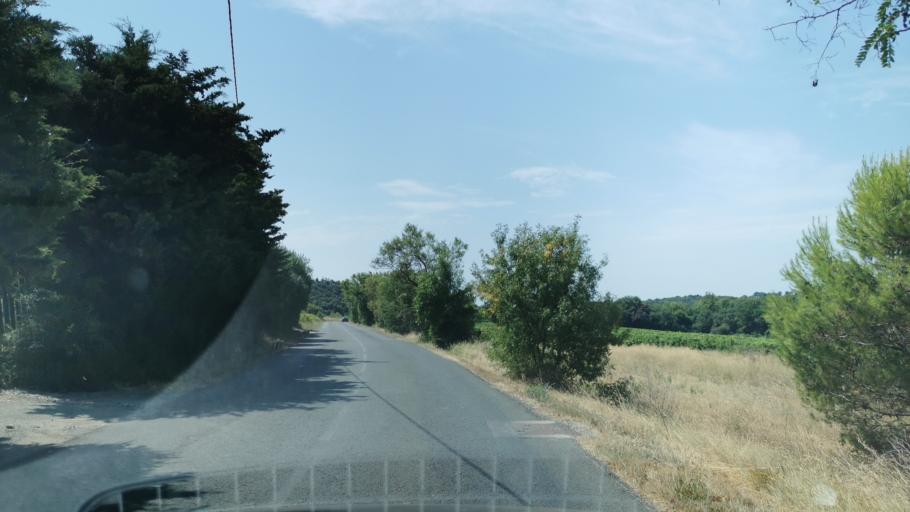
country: FR
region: Languedoc-Roussillon
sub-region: Departement de l'Aude
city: Bize-Minervois
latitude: 43.3082
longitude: 2.8710
